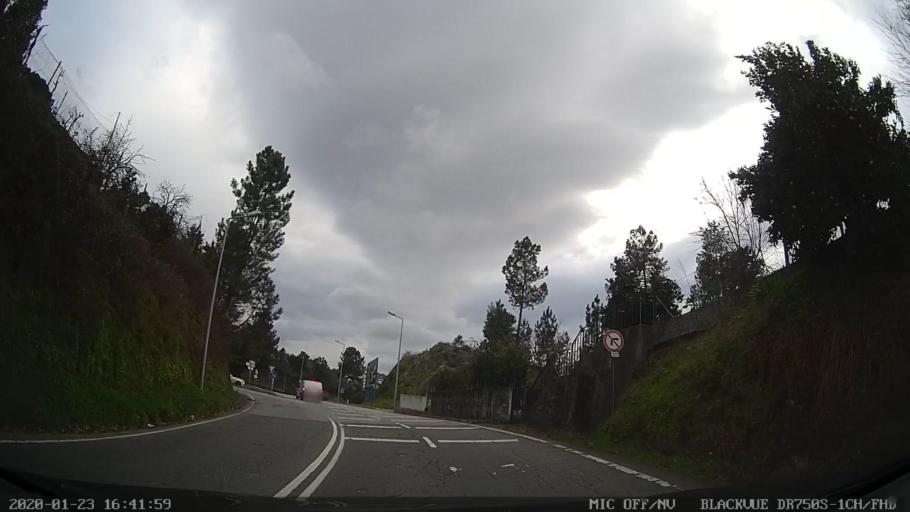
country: PT
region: Porto
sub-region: Amarante
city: Amarante
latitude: 41.2655
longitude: -8.0757
